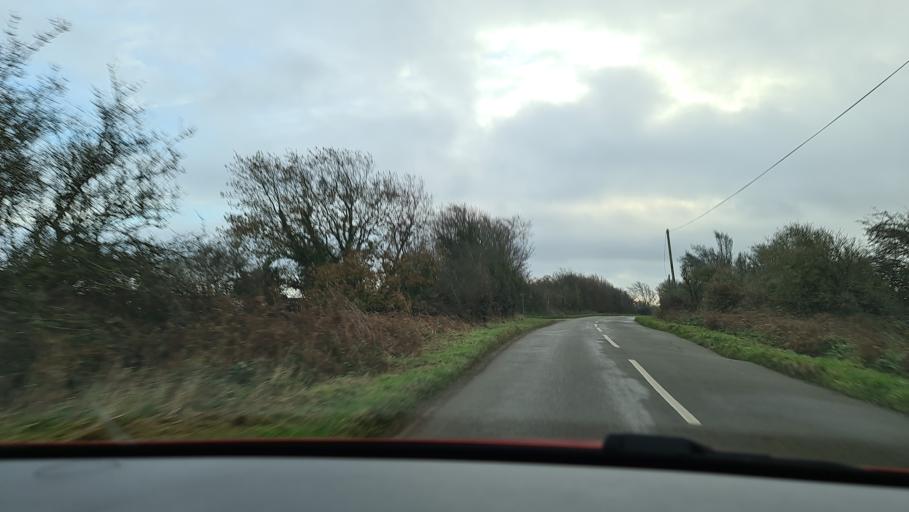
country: GB
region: England
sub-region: Buckinghamshire
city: Long Crendon
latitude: 51.8305
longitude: -1.0685
